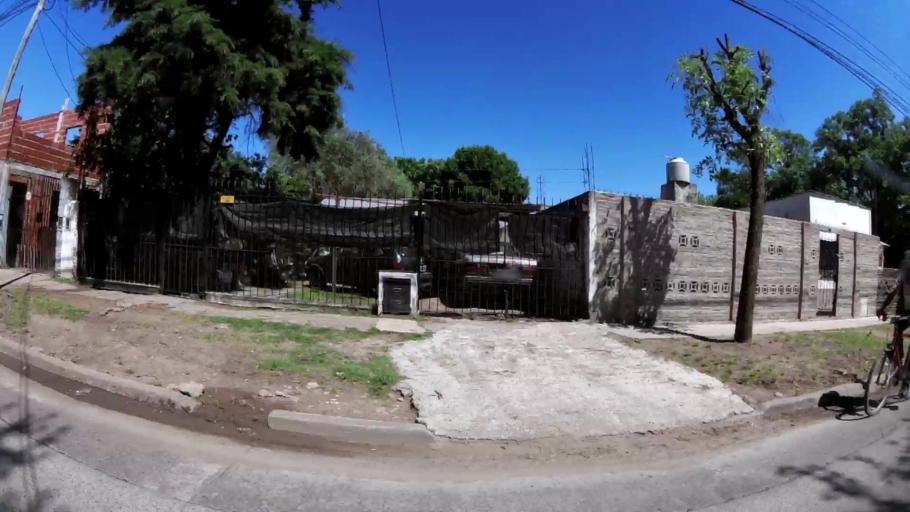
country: AR
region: Buenos Aires
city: Ituzaingo
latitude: -34.6703
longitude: -58.6610
